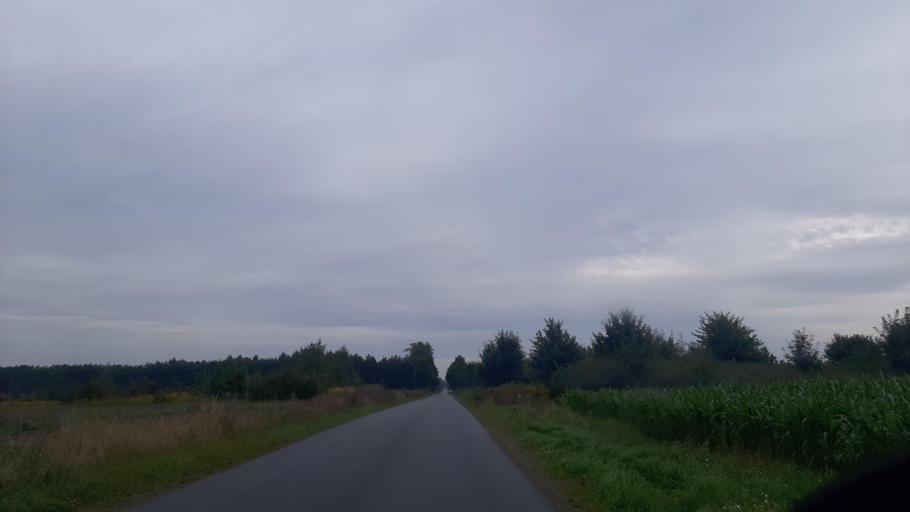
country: PL
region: Lublin Voivodeship
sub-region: Powiat lubartowski
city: Kamionka
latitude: 51.4675
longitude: 22.4407
